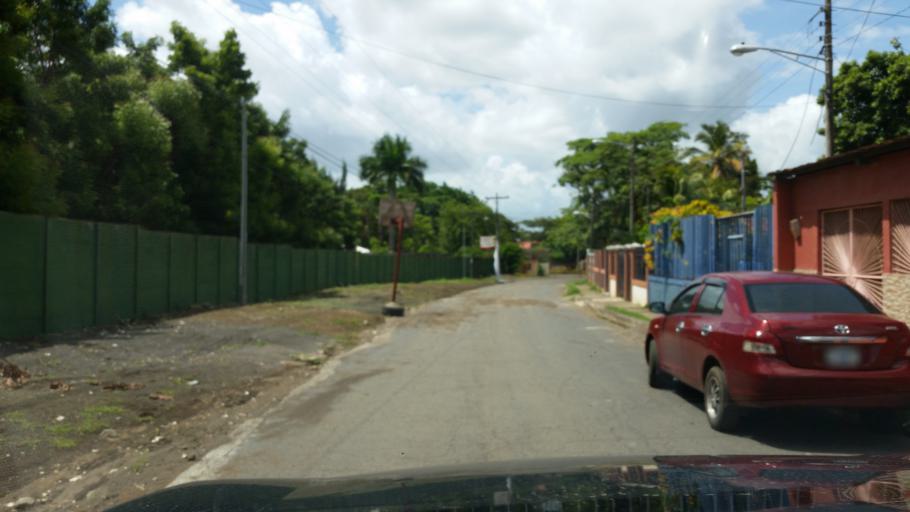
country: NI
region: Masaya
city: Ticuantepe
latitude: 12.0789
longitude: -86.2217
